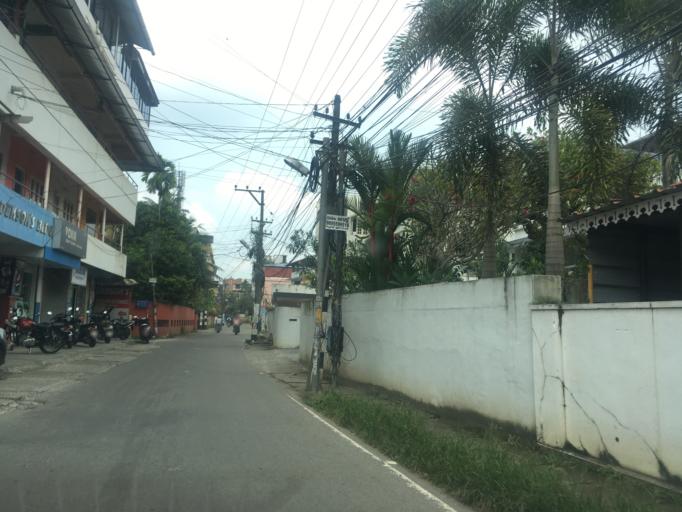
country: IN
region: Kerala
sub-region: Ernakulam
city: Elur
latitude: 10.0240
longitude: 76.3128
